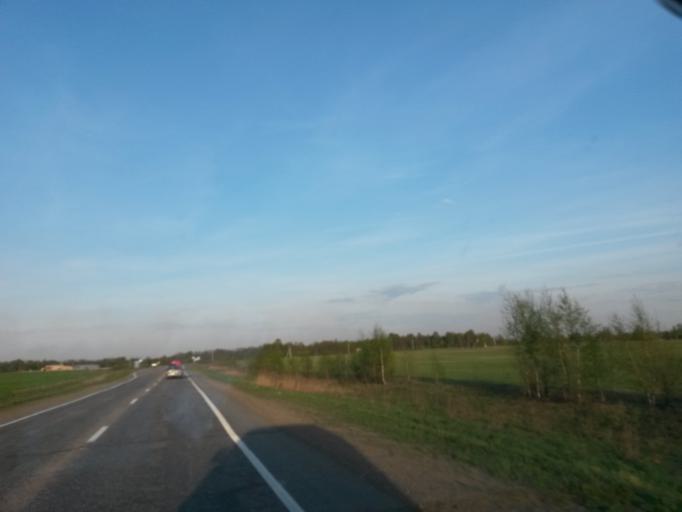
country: RU
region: Jaroslavl
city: Kurba
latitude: 57.6814
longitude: 39.5138
